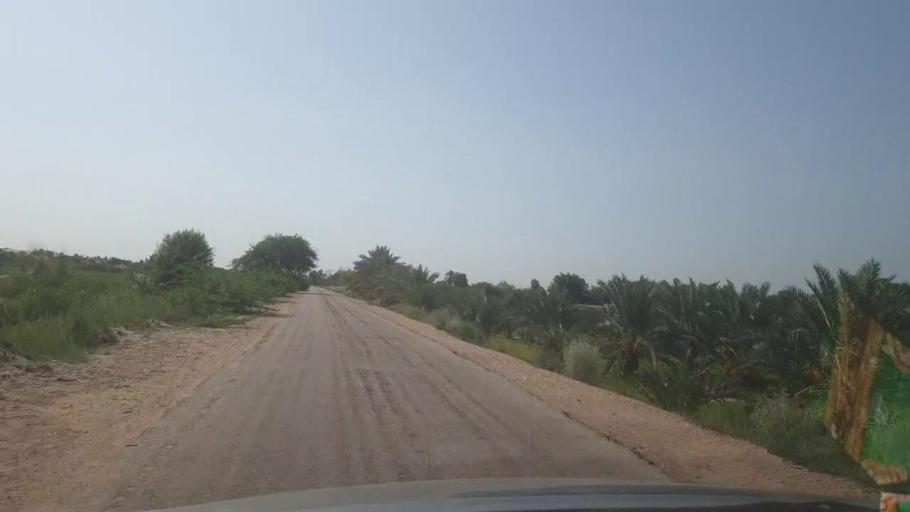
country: PK
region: Sindh
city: Rohri
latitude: 27.4643
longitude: 69.0396
